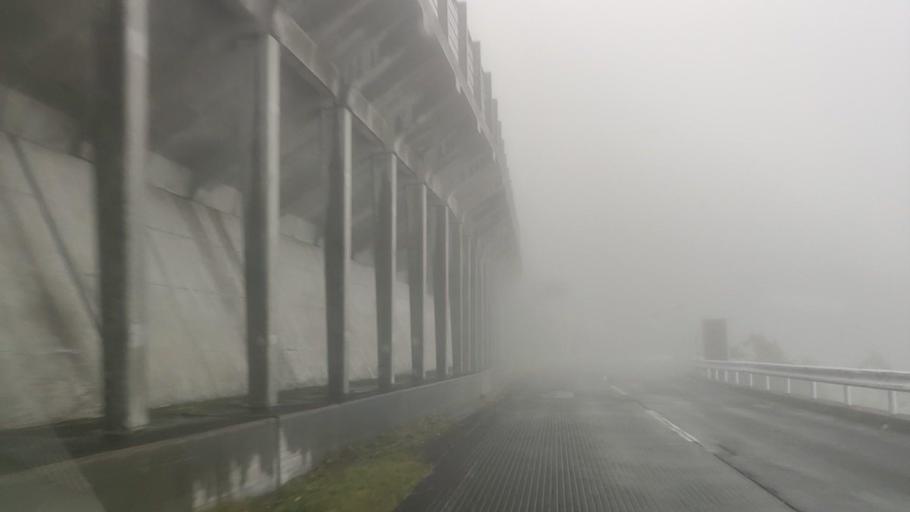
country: JP
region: Hokkaido
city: Date
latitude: 42.5507
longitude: 141.0838
